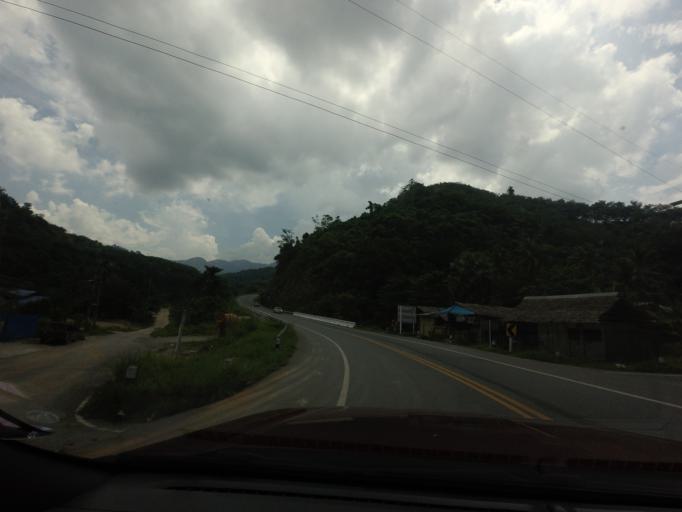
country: TH
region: Yala
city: Than To
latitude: 6.0513
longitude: 101.1973
